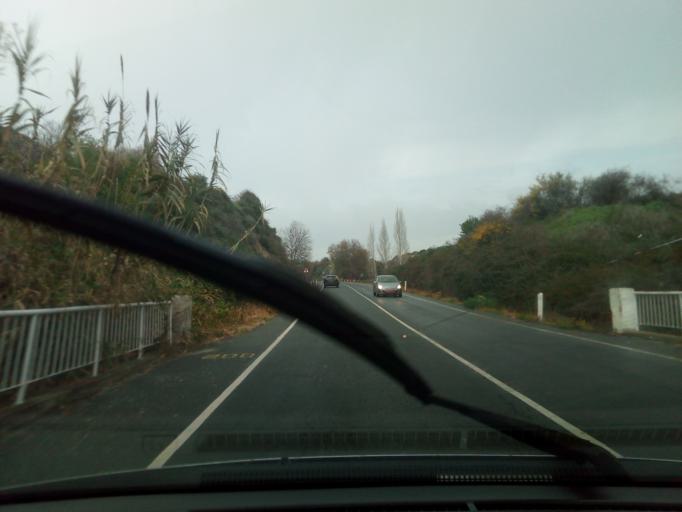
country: CY
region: Pafos
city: Polis
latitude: 34.9686
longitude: 32.4539
